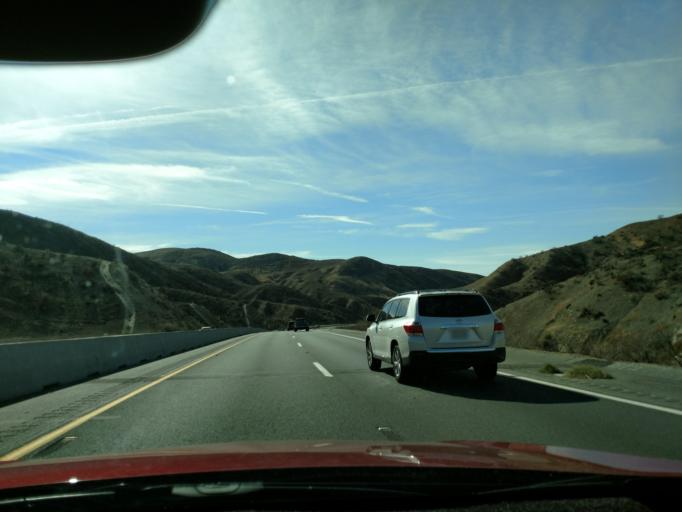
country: US
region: California
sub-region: Riverside County
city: Beaumont
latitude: 33.8743
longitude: -116.9927
